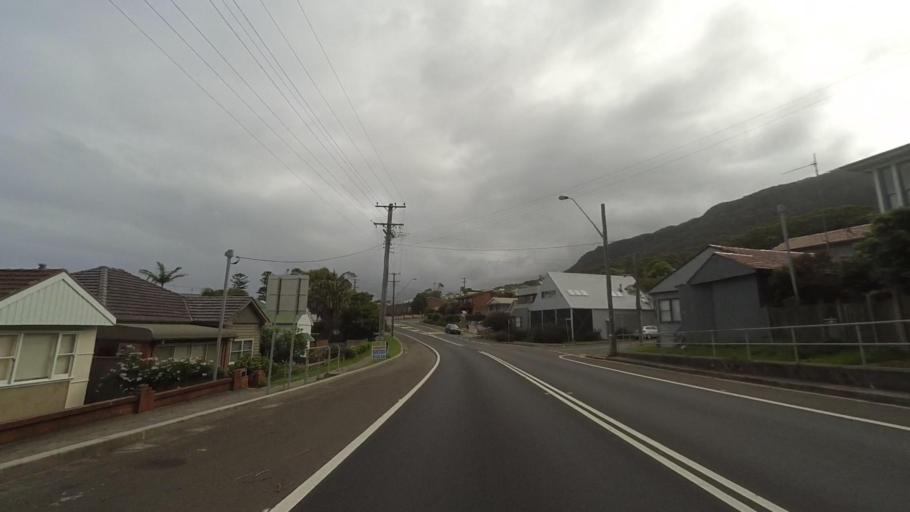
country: AU
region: New South Wales
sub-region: Wollongong
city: Bulli
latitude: -34.2901
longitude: 150.9455
